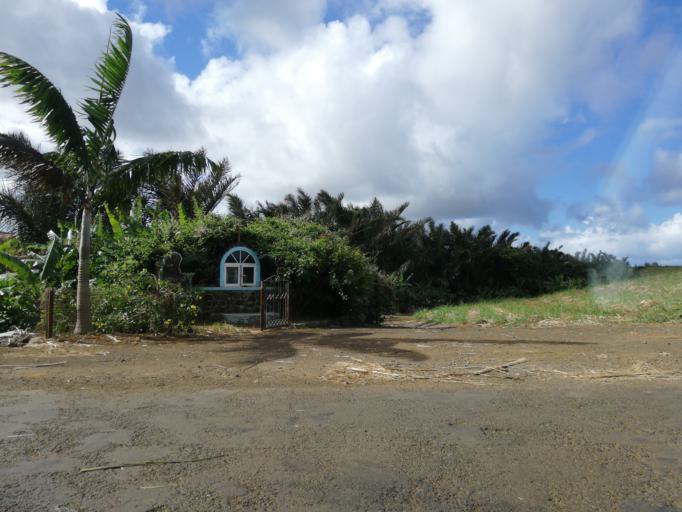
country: MU
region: Flacq
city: Bel Air Riviere Seche
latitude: -20.2797
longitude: 57.7445
